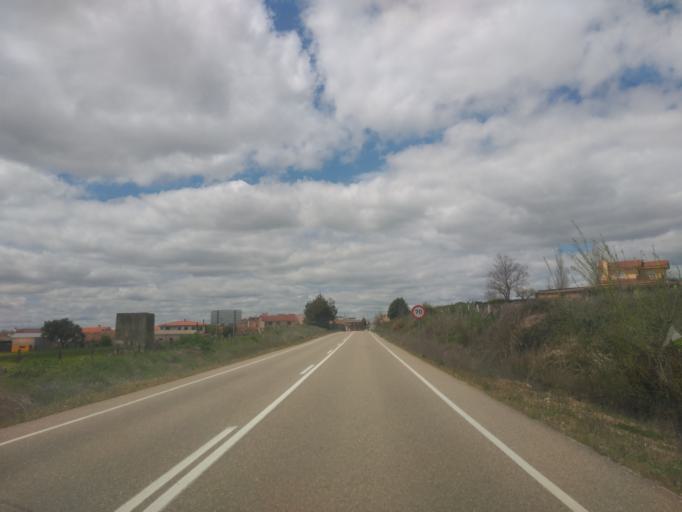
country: ES
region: Castille and Leon
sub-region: Provincia de Salamanca
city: Valverdon
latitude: 41.0458
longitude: -5.7655
